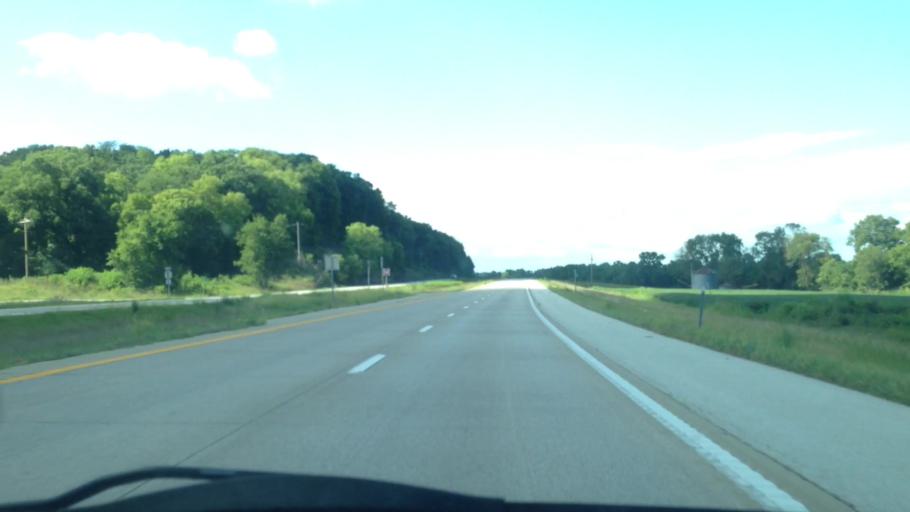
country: US
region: Missouri
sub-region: Lewis County
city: Canton
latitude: 40.2282
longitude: -91.5300
